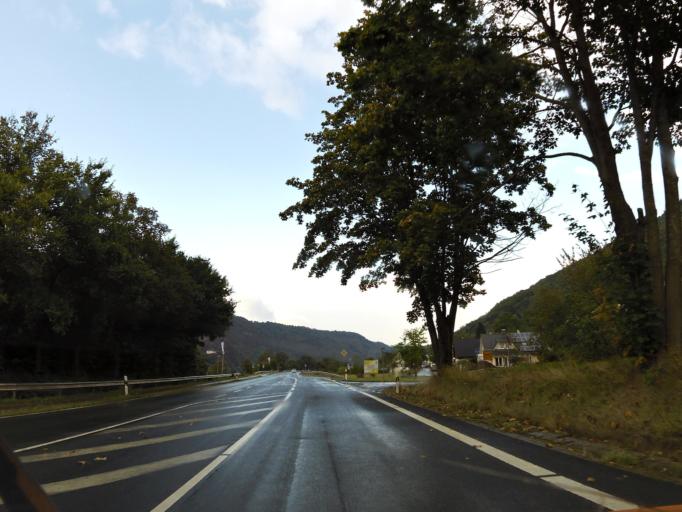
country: DE
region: Rheinland-Pfalz
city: Burgen
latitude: 50.2030
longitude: 7.3811
